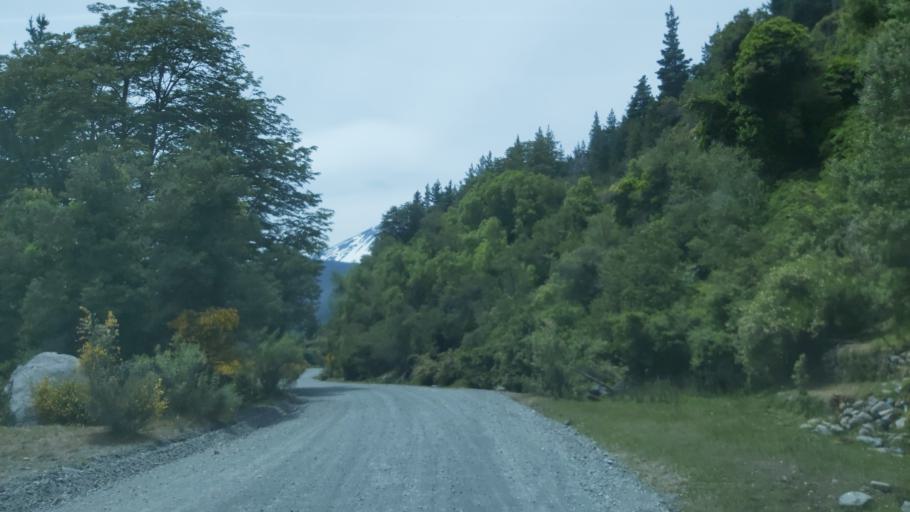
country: AR
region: Neuquen
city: Las Ovejas
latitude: -37.3968
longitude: -71.4533
